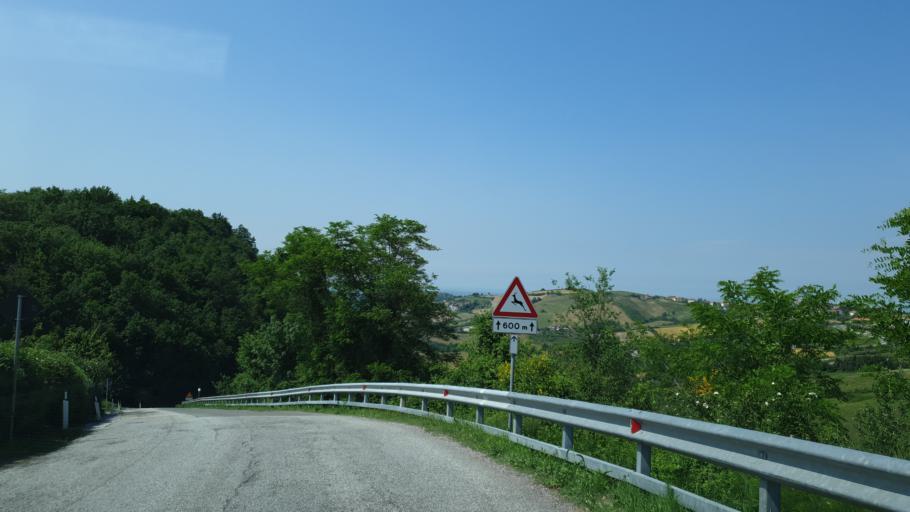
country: SM
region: San Marino
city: San Marino
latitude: 43.9378
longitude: 12.4335
